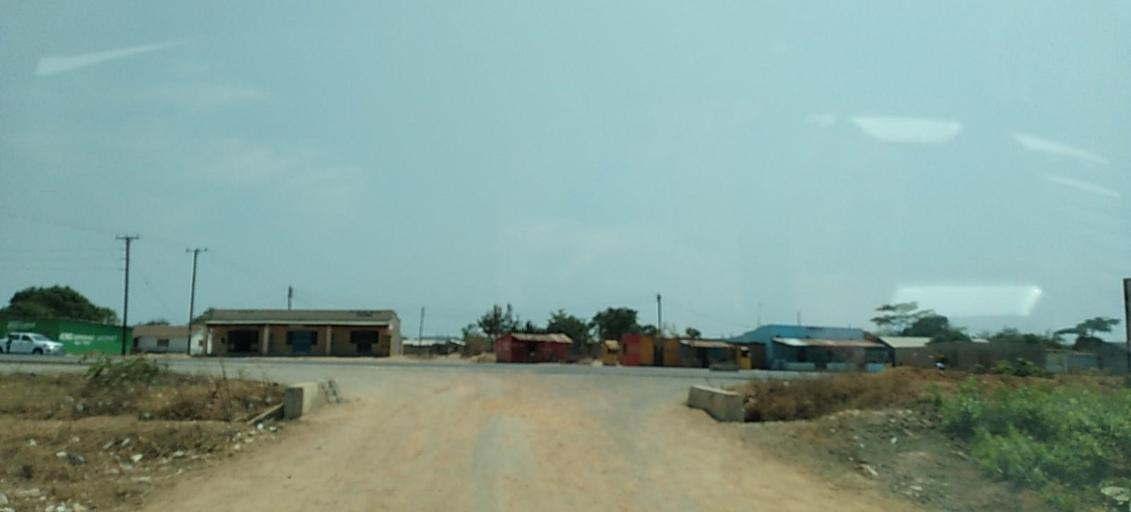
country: ZM
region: Copperbelt
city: Chingola
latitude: -12.5965
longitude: 27.9574
